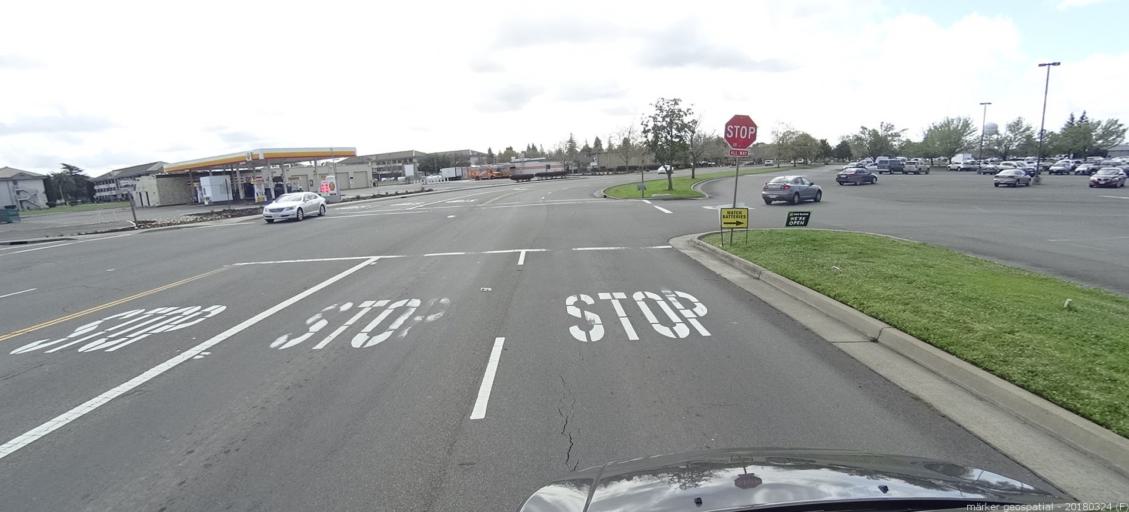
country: US
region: California
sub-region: Sacramento County
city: North Highlands
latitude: 38.6680
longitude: -121.3874
